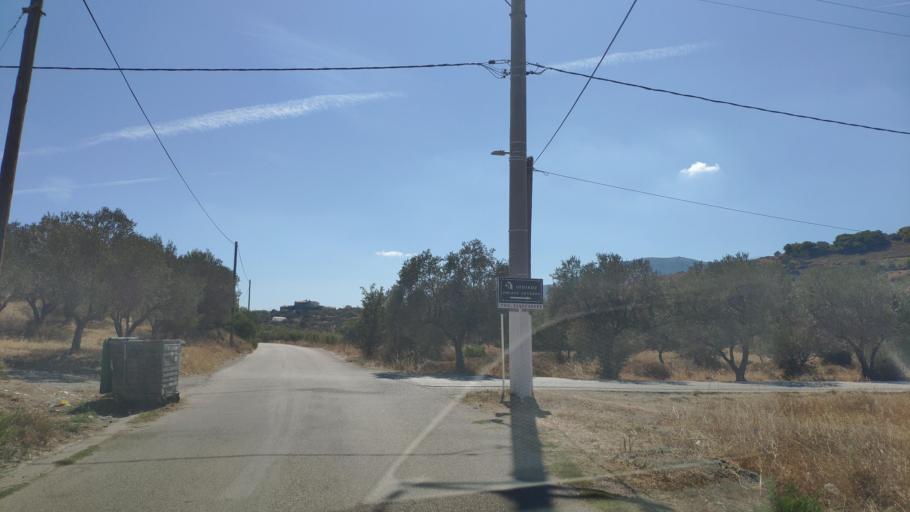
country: GR
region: Attica
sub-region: Nomarchia Anatolikis Attikis
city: Kouvaras
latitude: 37.8281
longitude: 23.9914
